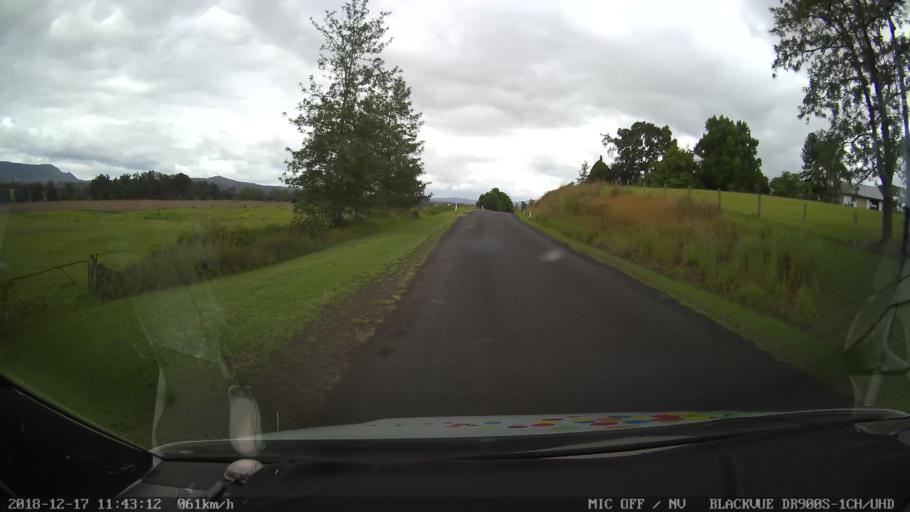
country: AU
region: New South Wales
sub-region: Kyogle
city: Kyogle
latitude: -28.6622
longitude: 152.5927
